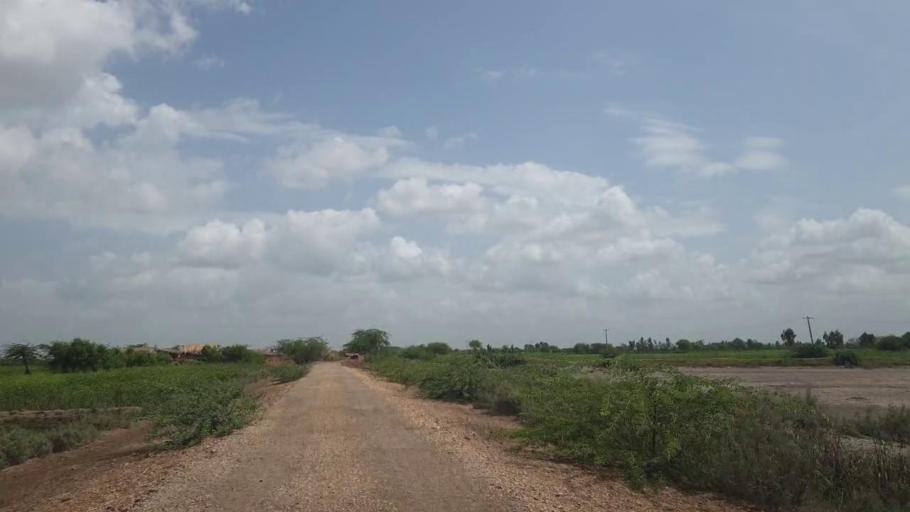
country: PK
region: Sindh
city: Tando Bago
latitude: 24.6566
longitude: 68.9926
